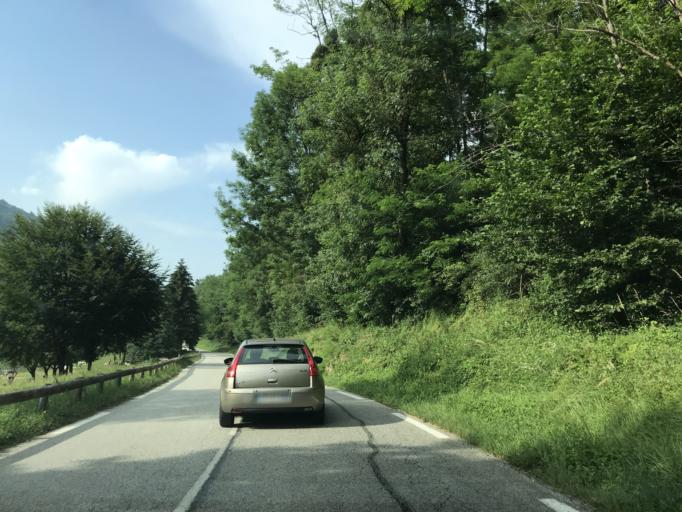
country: FR
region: Rhone-Alpes
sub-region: Departement de l'Isere
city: Allevard
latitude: 45.4071
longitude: 6.0863
